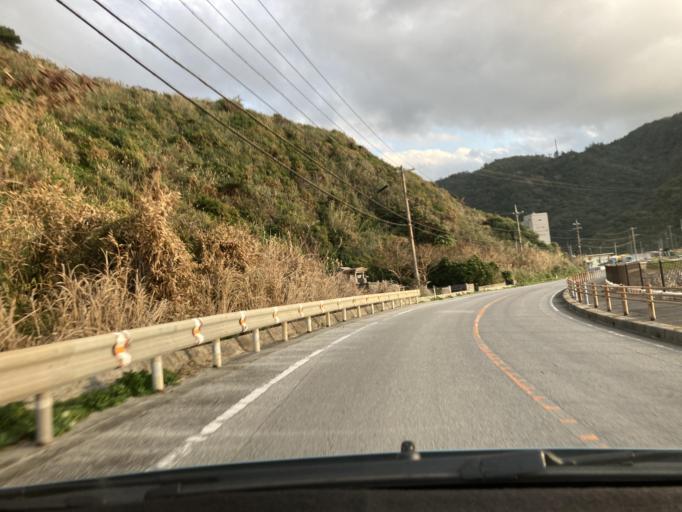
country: JP
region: Okinawa
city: Nago
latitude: 26.8004
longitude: 128.2323
